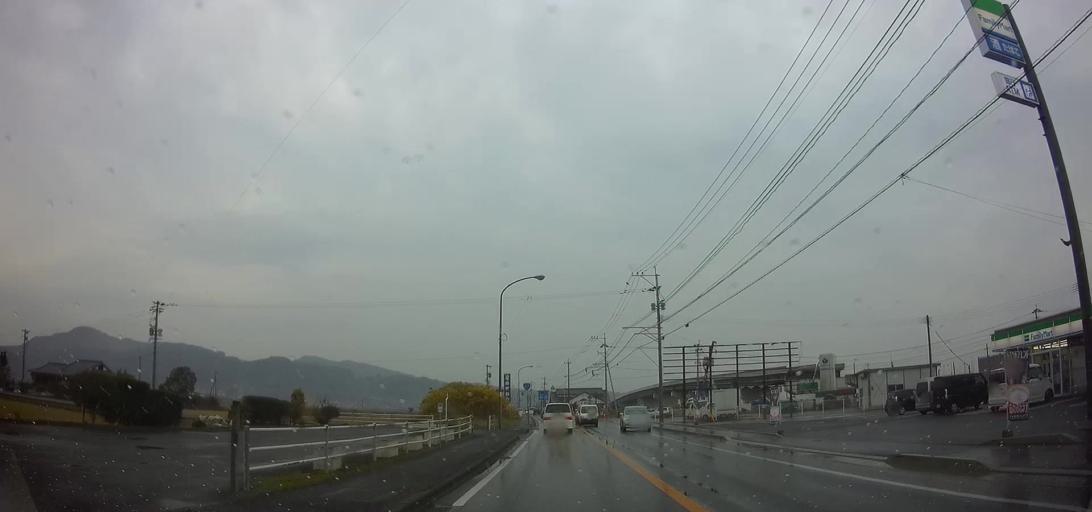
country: JP
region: Nagasaki
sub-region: Isahaya-shi
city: Isahaya
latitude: 32.8343
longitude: 130.1268
